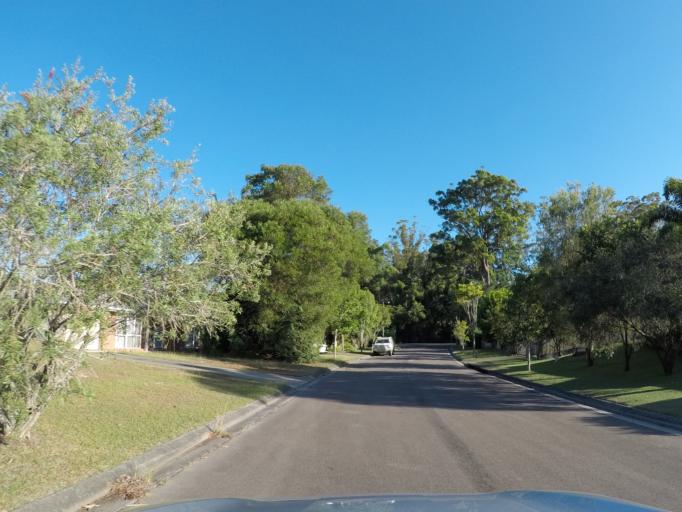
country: AU
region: Queensland
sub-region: Sunshine Coast
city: Nambour
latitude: -26.6203
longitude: 152.8605
